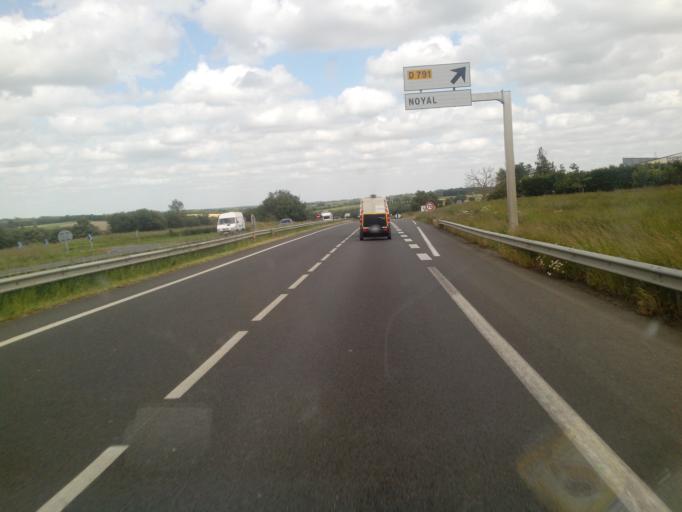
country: FR
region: Brittany
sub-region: Departement des Cotes-d'Armor
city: Lamballe
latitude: 48.4551
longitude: -2.4981
